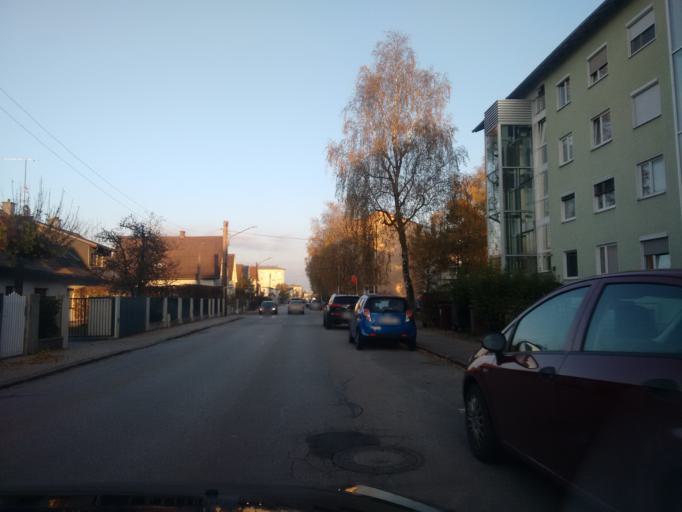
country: AT
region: Upper Austria
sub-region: Wels Stadt
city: Wels
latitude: 48.1599
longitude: 14.0038
